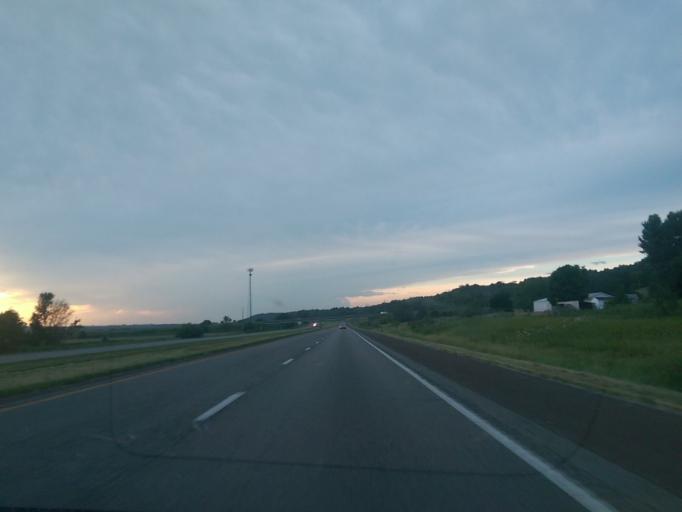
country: US
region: Missouri
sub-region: Holt County
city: Mound City
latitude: 40.2043
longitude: -95.3709
